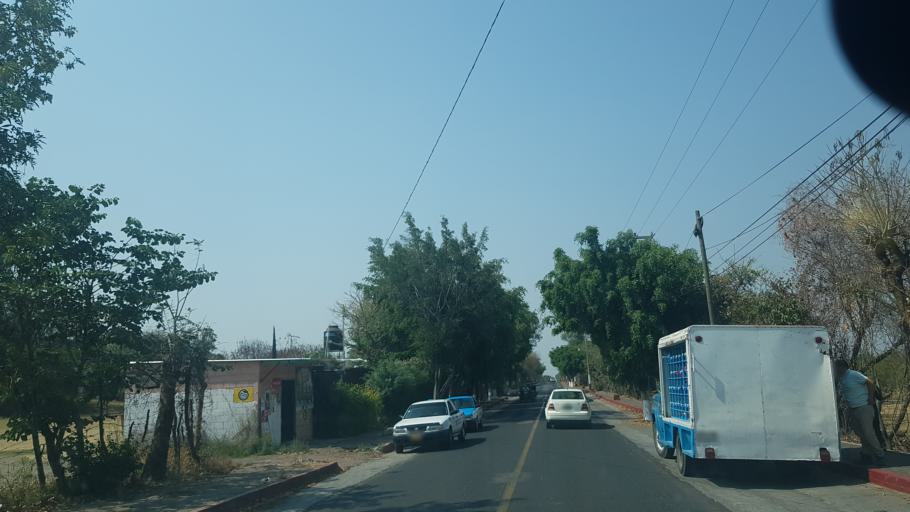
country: MX
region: Morelos
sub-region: Zacualpan
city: Zacualpan de Amilpas
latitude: 18.7856
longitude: -98.7709
